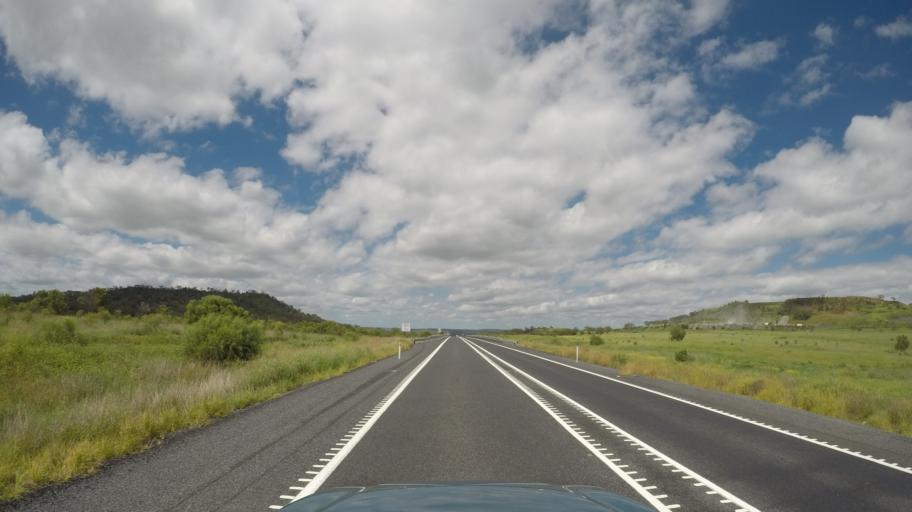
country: AU
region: Queensland
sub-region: Toowoomba
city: Westbrook
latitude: -27.5535
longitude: 151.8257
